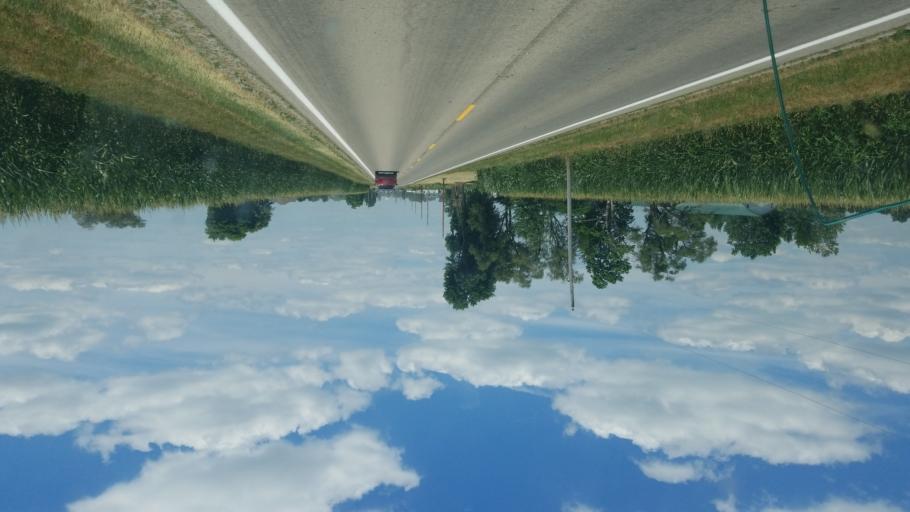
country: US
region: Ohio
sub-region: Defiance County
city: Hicksville
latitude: 41.2765
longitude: -84.7936
